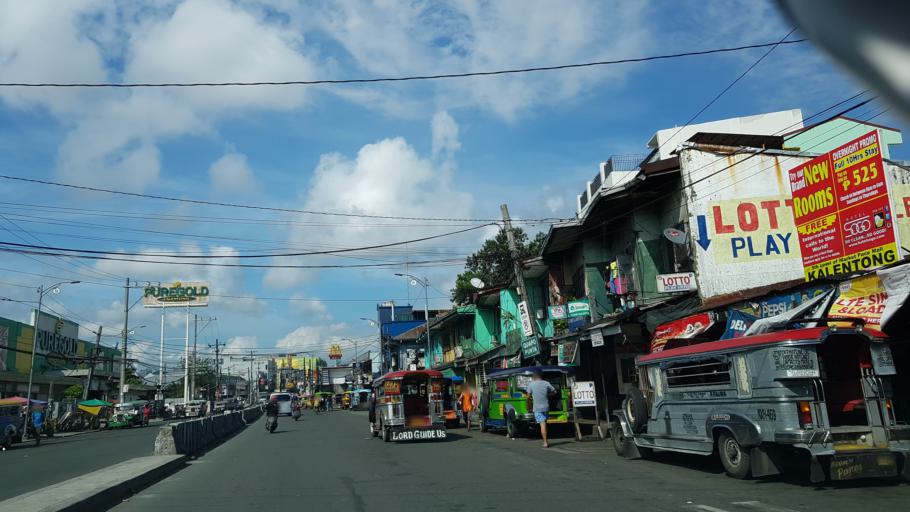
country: PH
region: Metro Manila
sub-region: San Juan
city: San Juan
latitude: 14.5877
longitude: 121.0212
